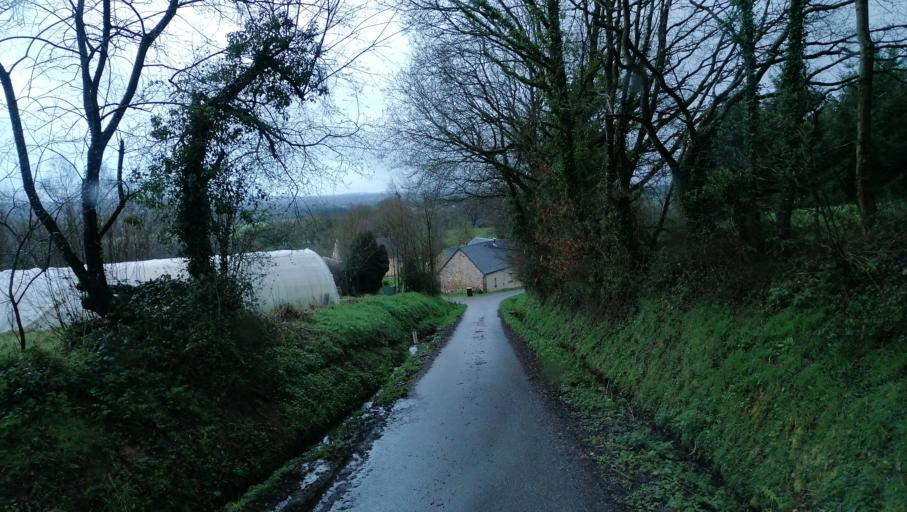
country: FR
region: Brittany
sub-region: Departement des Cotes-d'Armor
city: Plouagat
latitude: 48.4810
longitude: -2.9869
